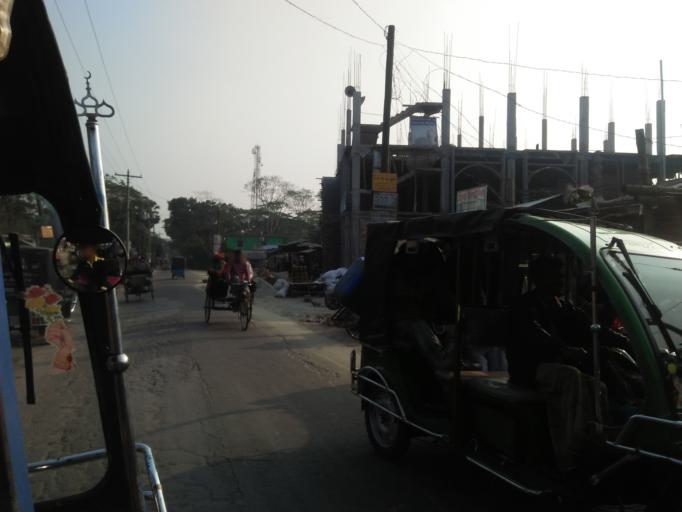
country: BD
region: Barisal
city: Bhola
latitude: 22.7271
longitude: 90.6349
